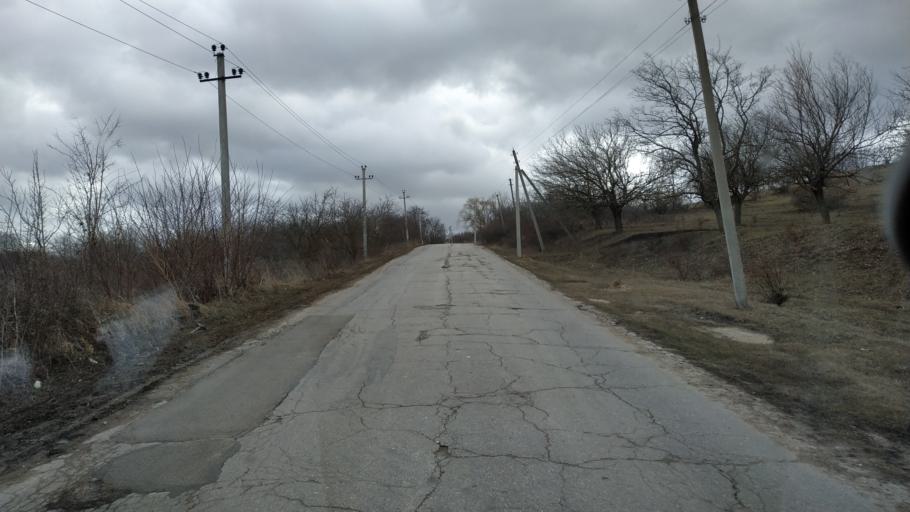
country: MD
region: Stinga Nistrului
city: Bucovat
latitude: 47.2238
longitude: 28.4257
